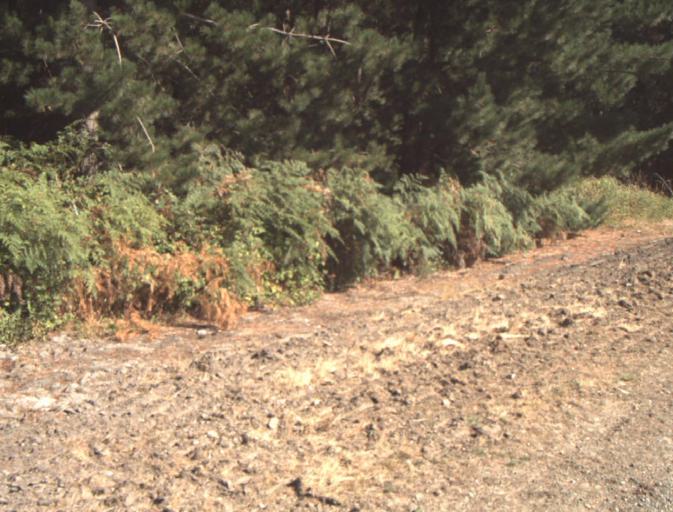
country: AU
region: Tasmania
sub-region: Launceston
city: Mayfield
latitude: -41.1652
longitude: 147.2123
